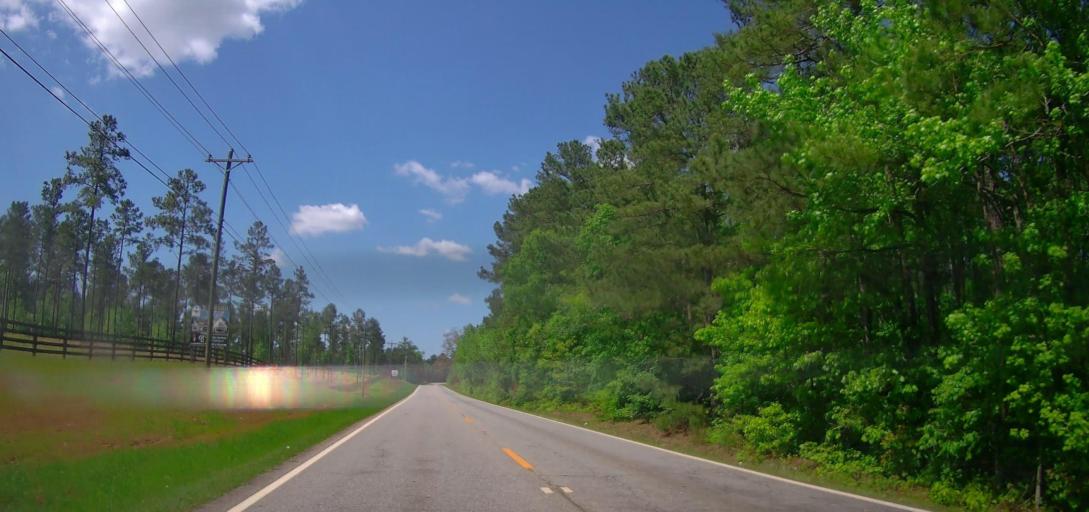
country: US
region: Georgia
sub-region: Putnam County
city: Eatonton
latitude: 33.2771
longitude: -83.3027
